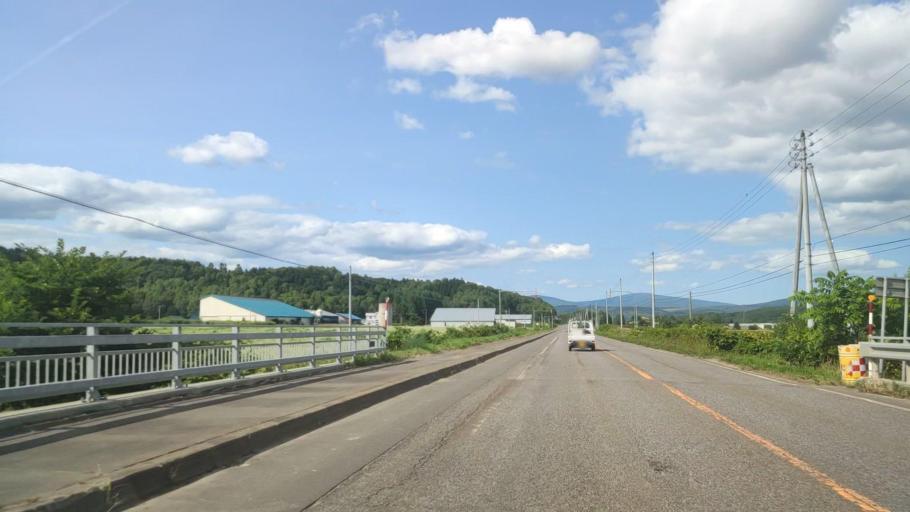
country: JP
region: Hokkaido
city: Nayoro
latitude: 44.3988
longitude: 142.3953
